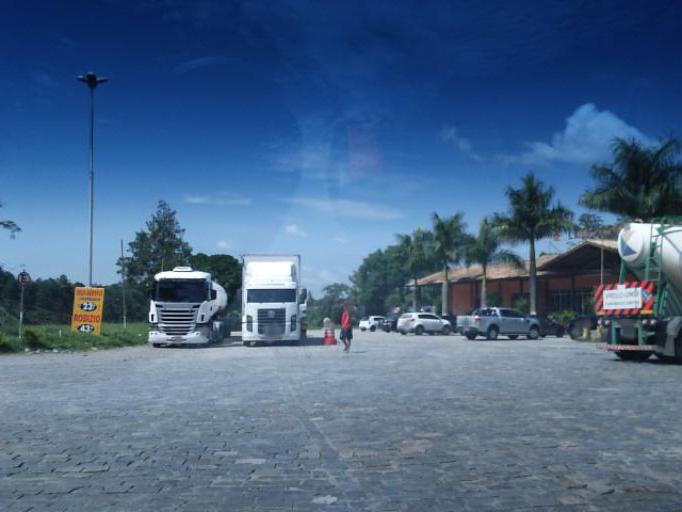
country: BR
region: Sao Paulo
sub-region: Itapecerica Da Serra
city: Itapecerica da Serra
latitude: -23.7157
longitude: -46.8808
